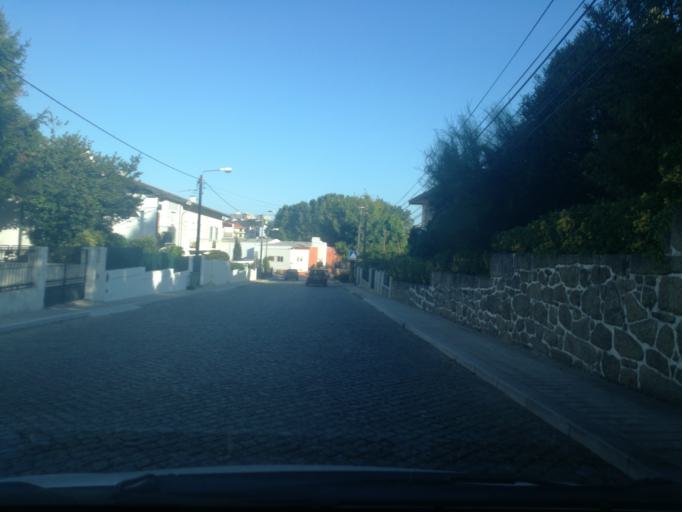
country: PT
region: Porto
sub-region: Maia
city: Milheiros
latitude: 41.2150
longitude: -8.5960
